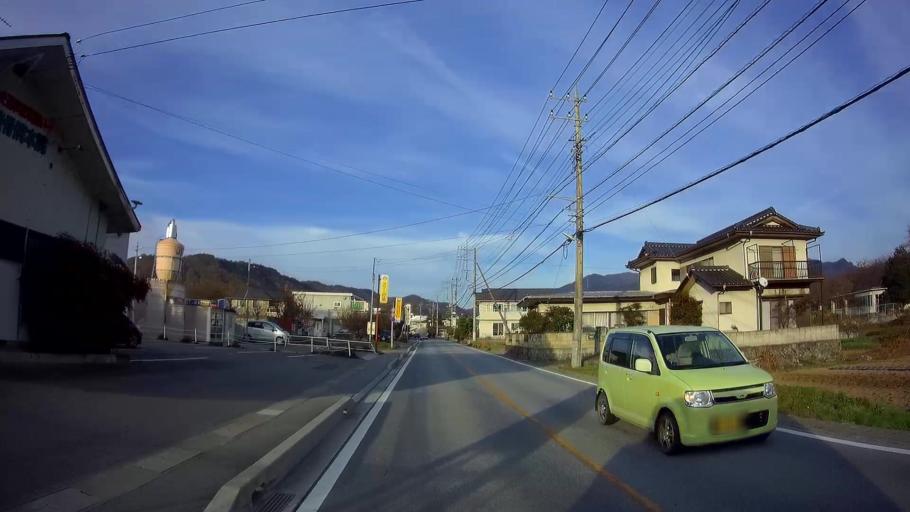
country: JP
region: Yamanashi
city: Ryuo
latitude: 35.4859
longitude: 138.4577
